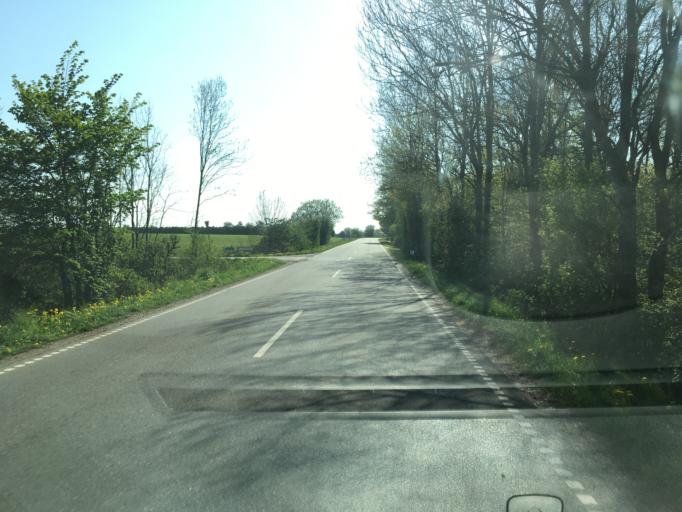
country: DK
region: South Denmark
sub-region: Haderslev Kommune
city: Vojens
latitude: 55.2965
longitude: 9.2491
